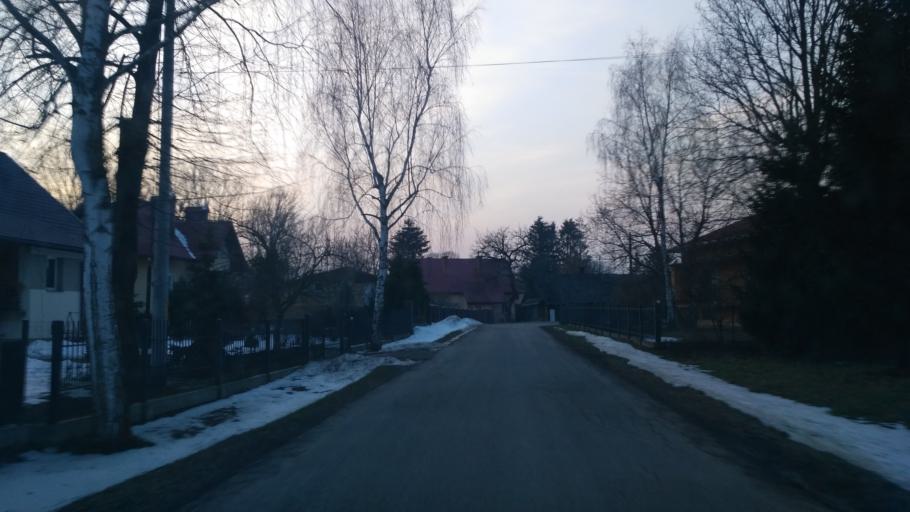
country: PL
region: Subcarpathian Voivodeship
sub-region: Powiat rzeszowski
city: Siedliska
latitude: 49.9678
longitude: 21.9672
